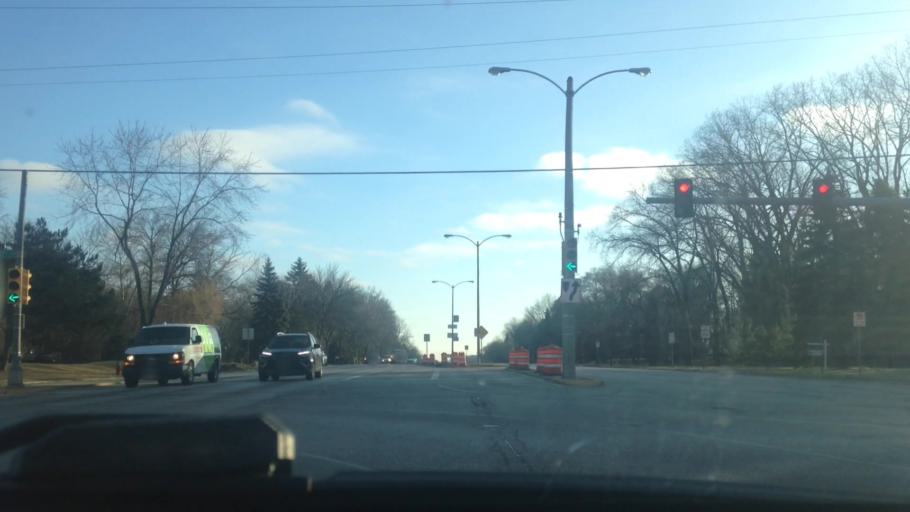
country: US
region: Wisconsin
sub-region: Waukesha County
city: Butler
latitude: 43.1484
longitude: -88.0453
